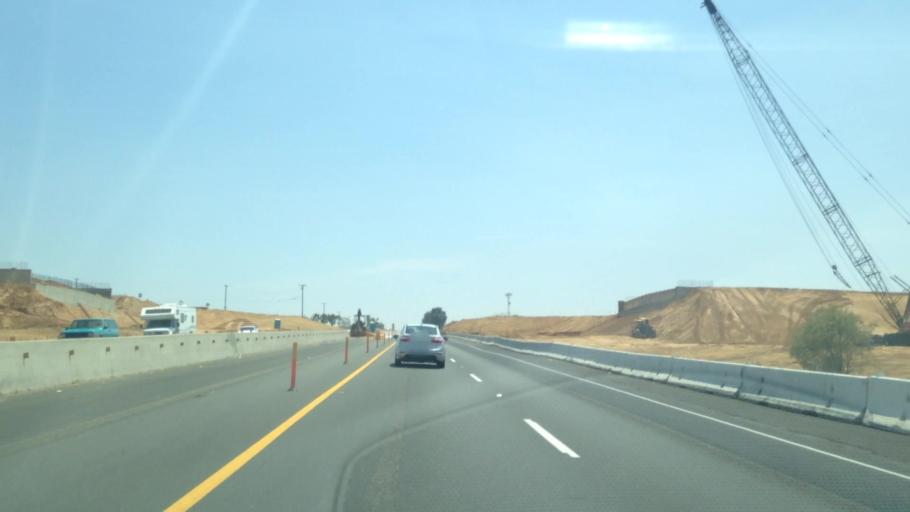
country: US
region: California
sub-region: Riverside County
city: Beaumont
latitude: 33.9336
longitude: -117.0185
